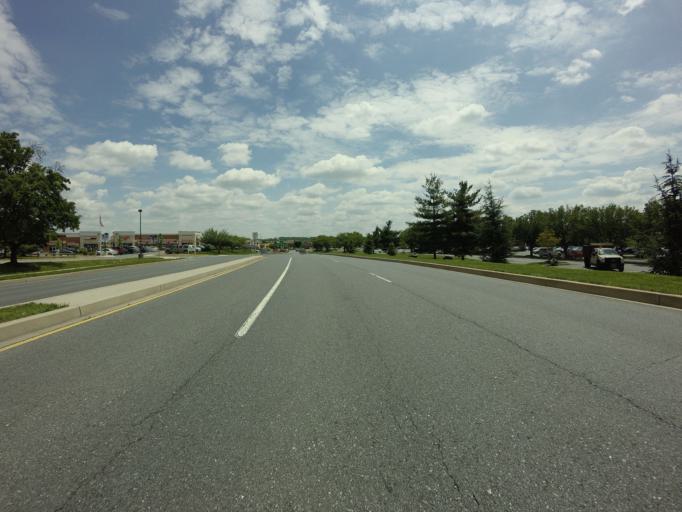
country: US
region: Maryland
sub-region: Frederick County
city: Frederick
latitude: 39.3852
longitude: -77.4064
